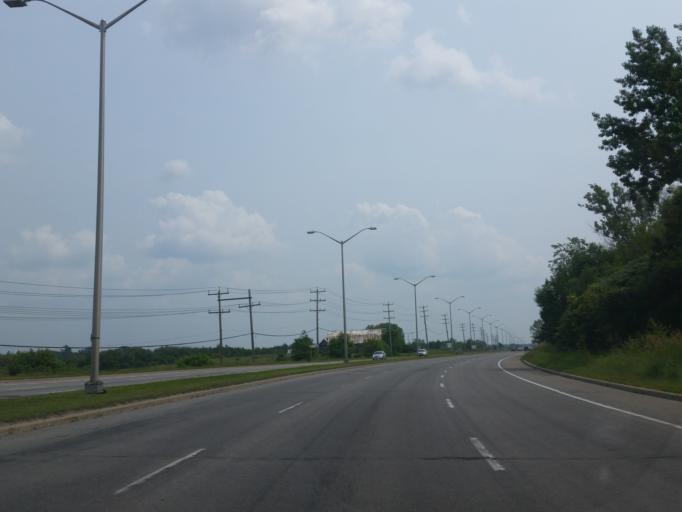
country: CA
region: Ontario
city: Bells Corners
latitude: 45.3314
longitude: -75.8928
